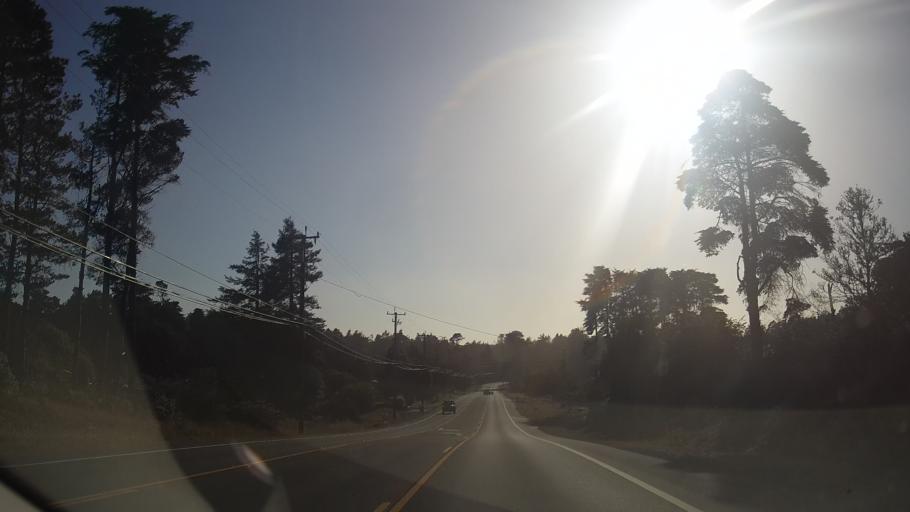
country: US
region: California
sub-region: Mendocino County
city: Fort Bragg
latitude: 39.4155
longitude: -123.7806
